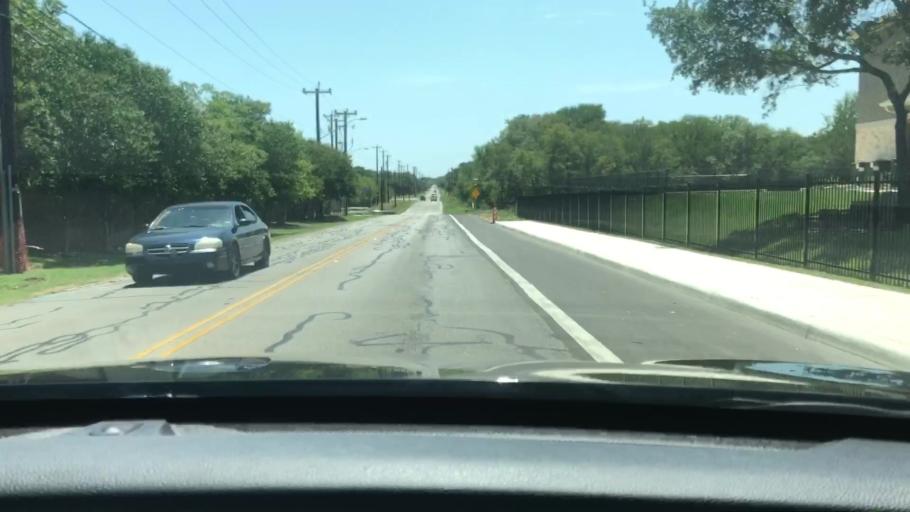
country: US
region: Texas
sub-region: Bexar County
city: Helotes
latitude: 29.5589
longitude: -98.6558
